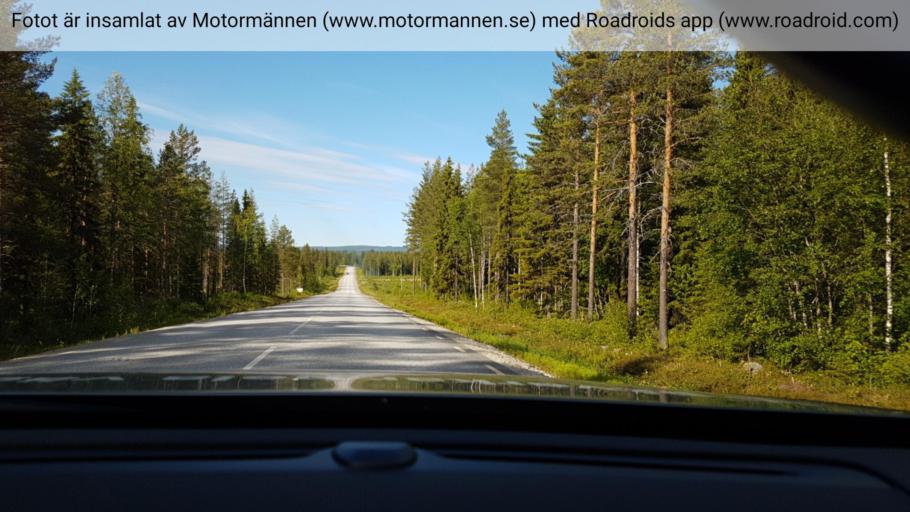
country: SE
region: Vaesterbotten
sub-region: Bjurholms Kommun
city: Bjurholm
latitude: 64.1657
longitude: 19.3825
